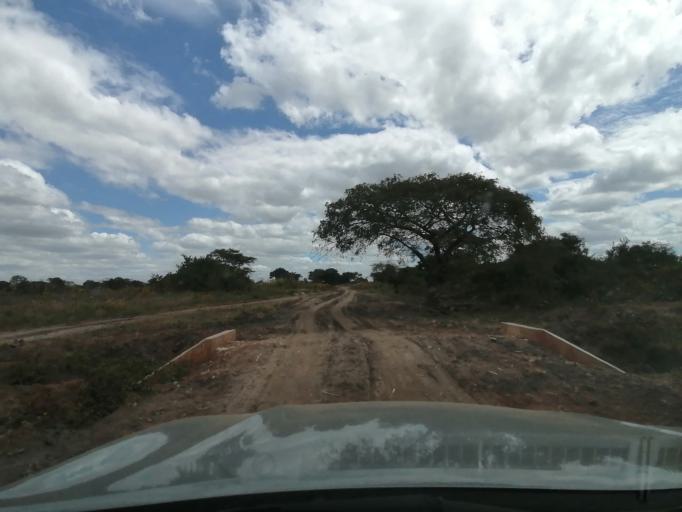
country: ZM
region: Central
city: Mumbwa
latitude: -14.5816
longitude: 27.2269
